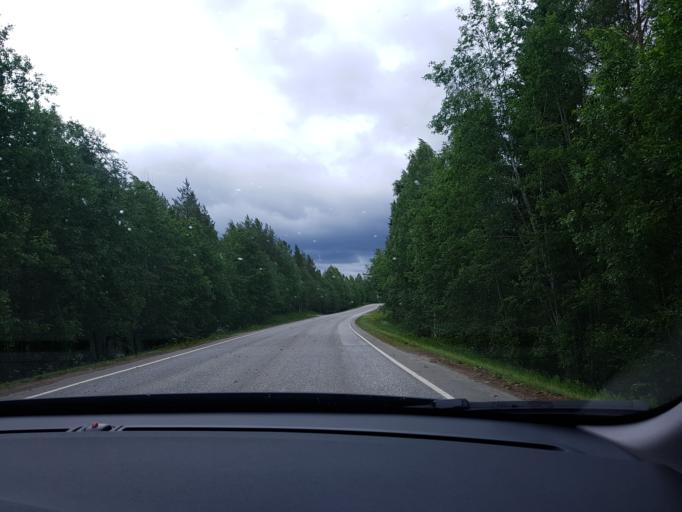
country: FI
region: Kainuu
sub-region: Kehys-Kainuu
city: Kuhmo
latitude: 64.1511
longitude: 29.4623
